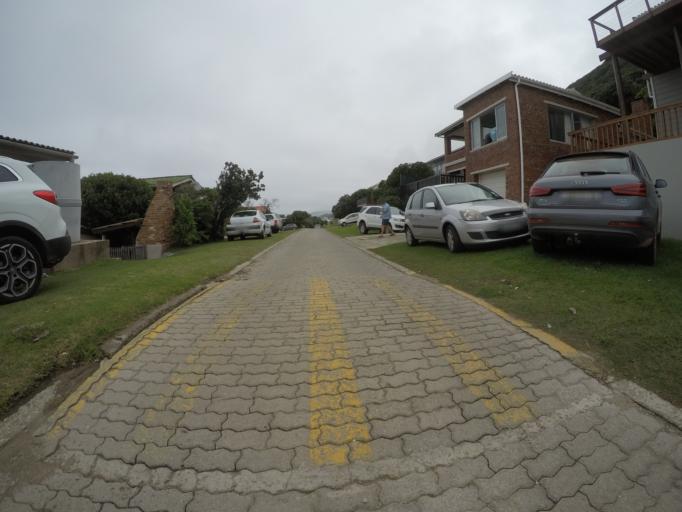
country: ZA
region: Eastern Cape
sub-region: Cacadu District Municipality
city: Kareedouw
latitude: -34.0714
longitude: 24.2199
